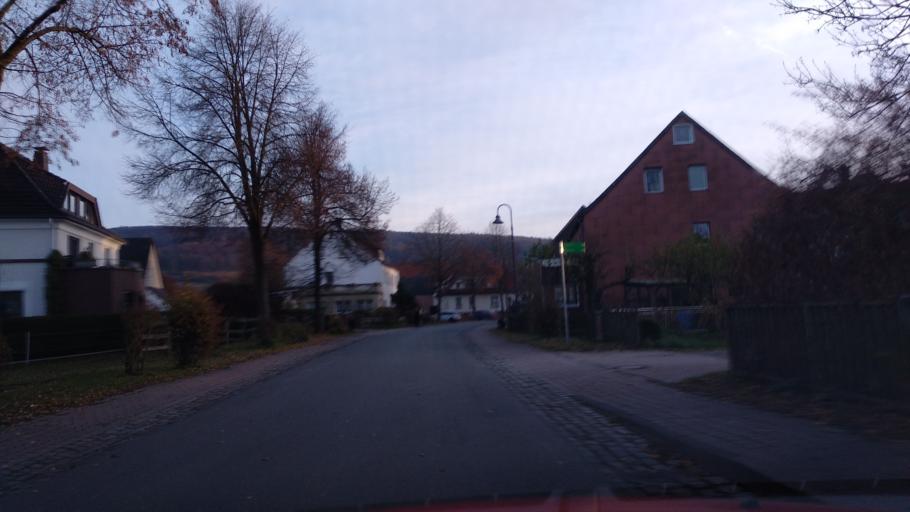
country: DE
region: Lower Saxony
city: Boffzen
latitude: 51.7141
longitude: 9.3432
